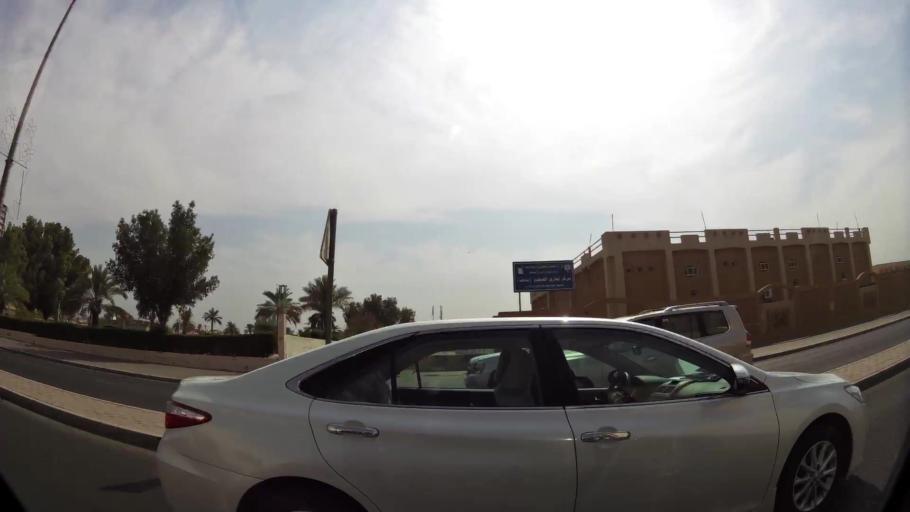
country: KW
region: Al Asimah
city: Ash Shamiyah
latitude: 29.3381
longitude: 47.9594
